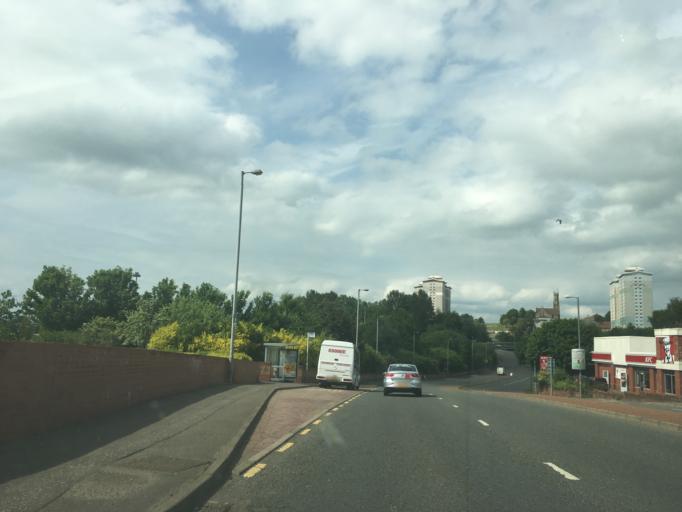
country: GB
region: Scotland
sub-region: North Lanarkshire
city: Coatbridge
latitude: 55.8567
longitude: -4.0204
